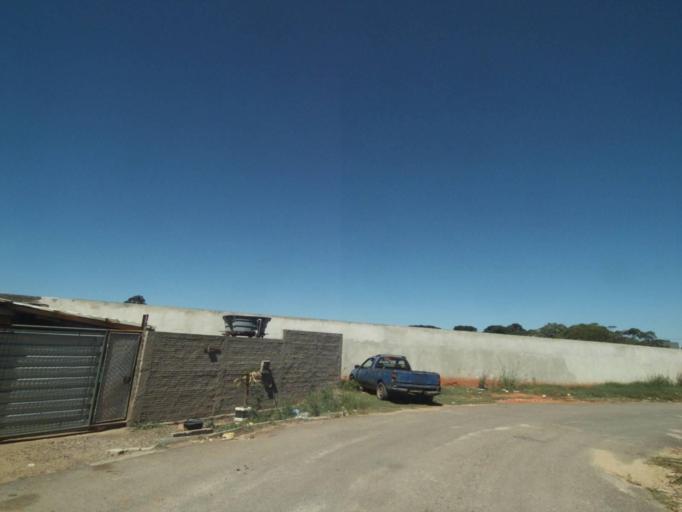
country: BR
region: Parana
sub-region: Curitiba
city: Curitiba
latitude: -25.4694
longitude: -49.3517
